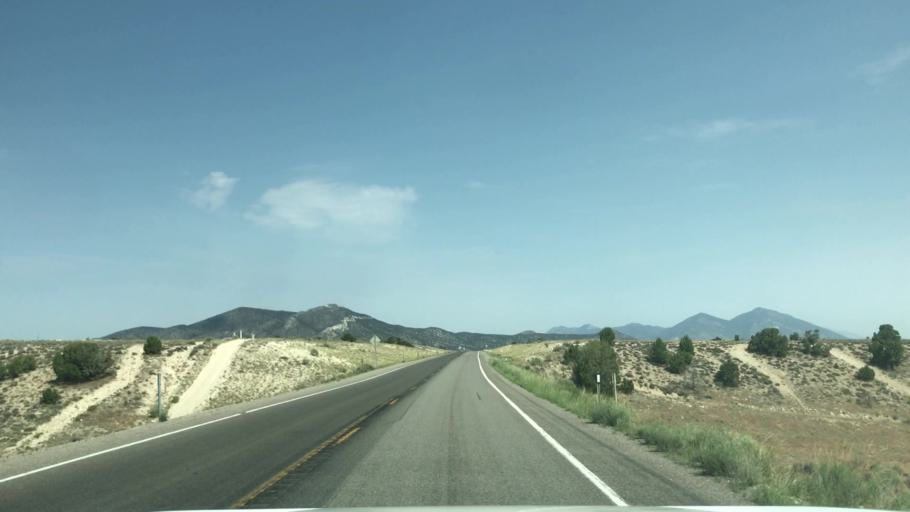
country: US
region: Nevada
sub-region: White Pine County
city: Ely
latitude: 39.2174
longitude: -114.8553
